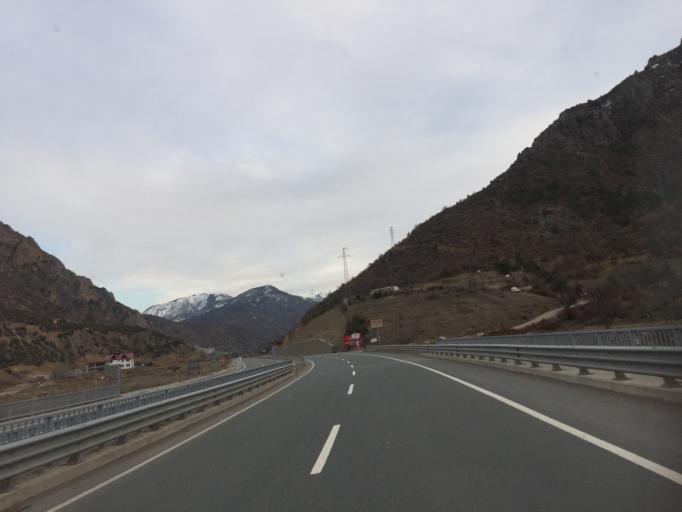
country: TR
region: Gumushane
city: Torul
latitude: 40.5368
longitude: 39.3277
